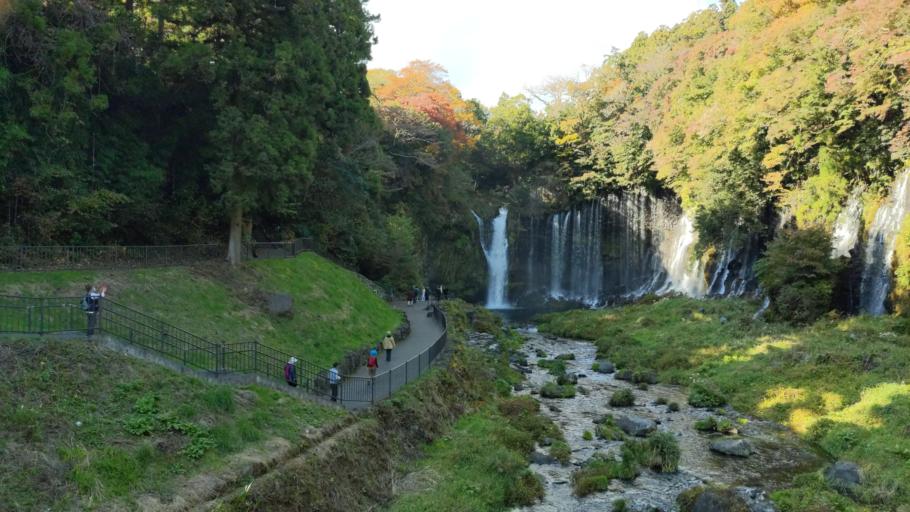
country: JP
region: Shizuoka
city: Fujinomiya
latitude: 35.3119
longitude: 138.5881
